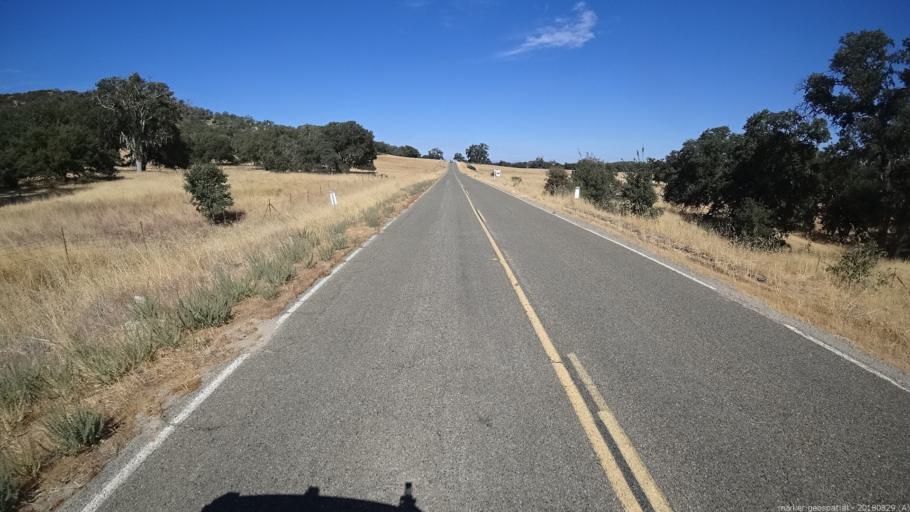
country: US
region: California
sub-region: San Luis Obispo County
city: Lake Nacimiento
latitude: 35.8225
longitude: -121.0118
